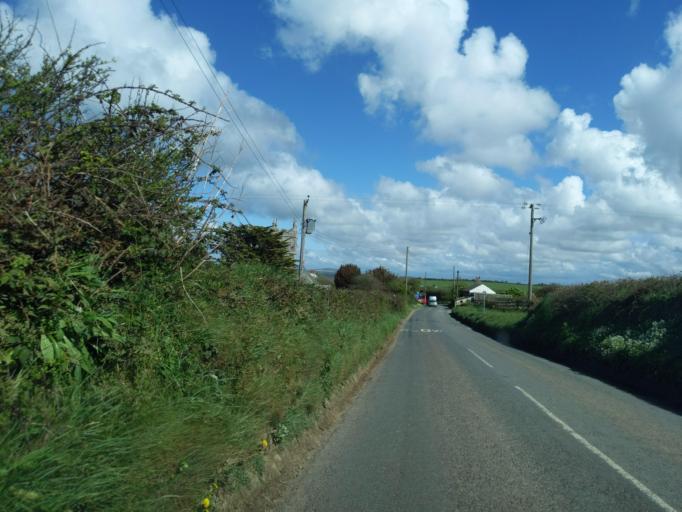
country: GB
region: England
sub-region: Cornwall
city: Wadebridge
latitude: 50.5730
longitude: -4.8322
